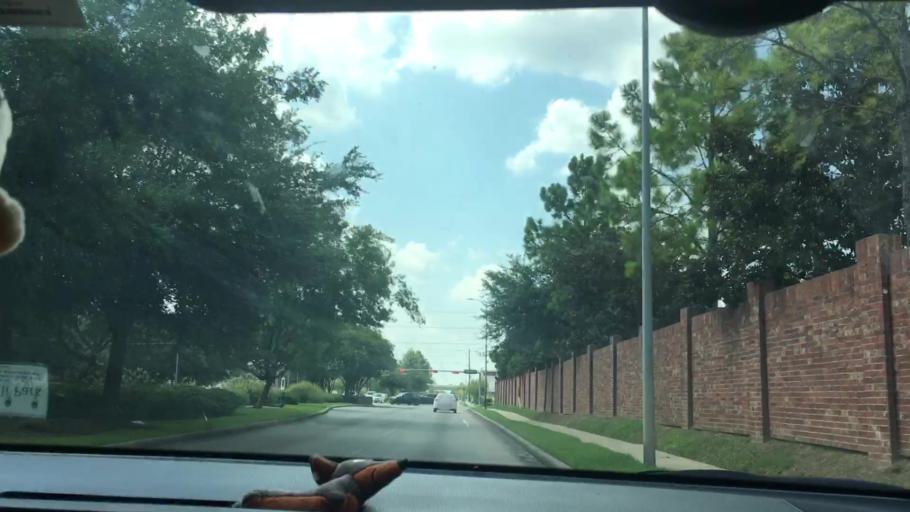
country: US
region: Texas
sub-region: Harris County
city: Bunker Hill Village
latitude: 29.7216
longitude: -95.5717
